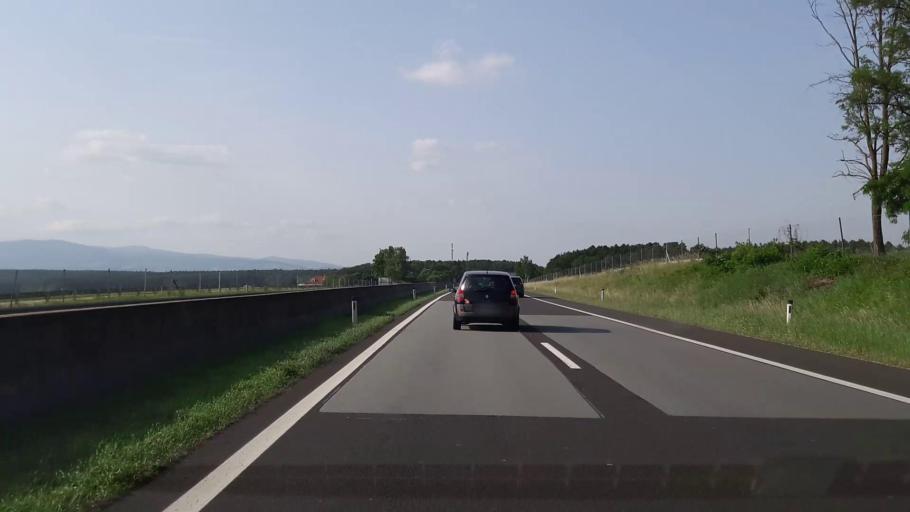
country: AT
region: Burgenland
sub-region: Politischer Bezirk Oberwart
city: Grafenschachen
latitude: 47.3265
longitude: 16.0611
